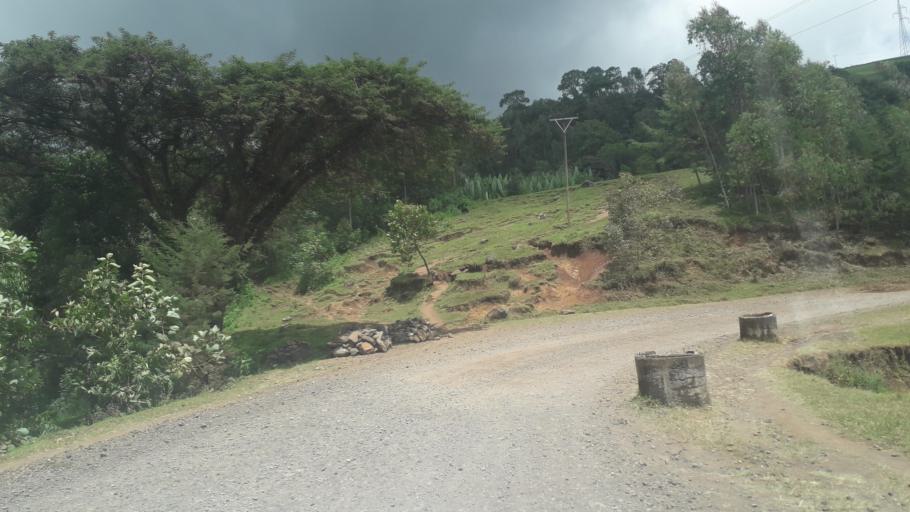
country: ET
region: Oromiya
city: Jima
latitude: 7.4303
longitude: 36.8732
